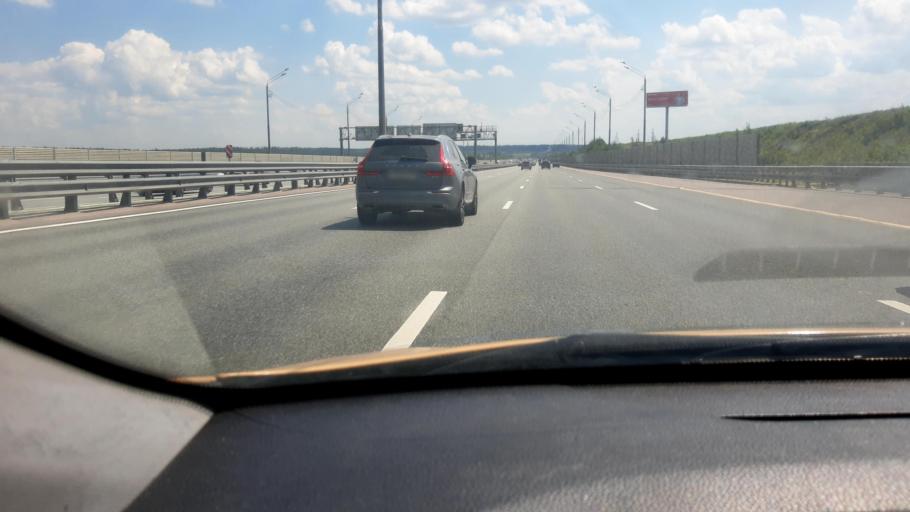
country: RU
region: Moskovskaya
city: Pavlovskaya Sloboda
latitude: 55.8017
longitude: 37.0403
